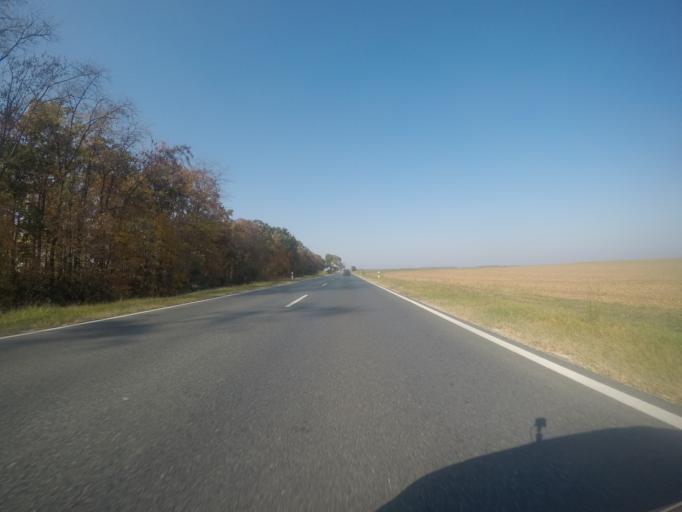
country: HU
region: Tolna
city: Madocsa
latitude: 46.7103
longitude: 18.8875
